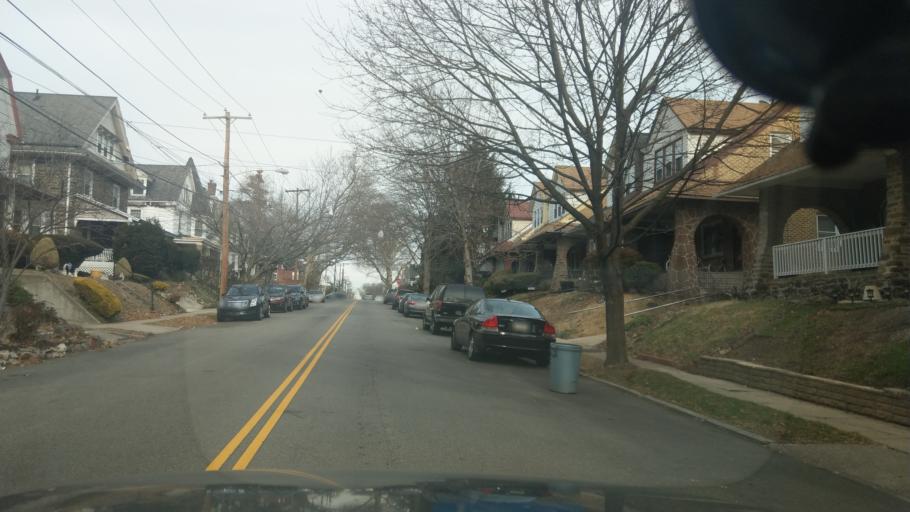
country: US
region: Pennsylvania
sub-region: Montgomery County
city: Wyncote
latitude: 40.0493
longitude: -75.1403
